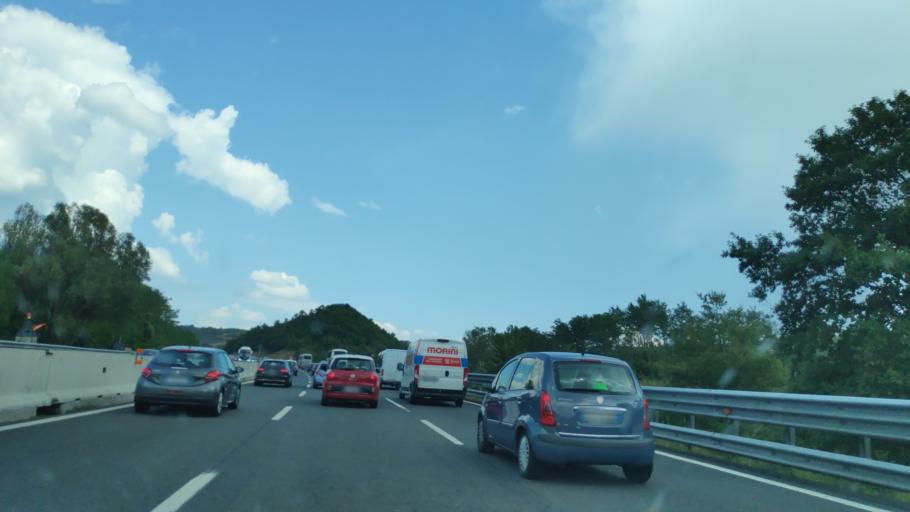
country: IT
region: Umbria
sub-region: Provincia di Terni
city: Ficulle
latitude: 42.8225
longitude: 12.0388
